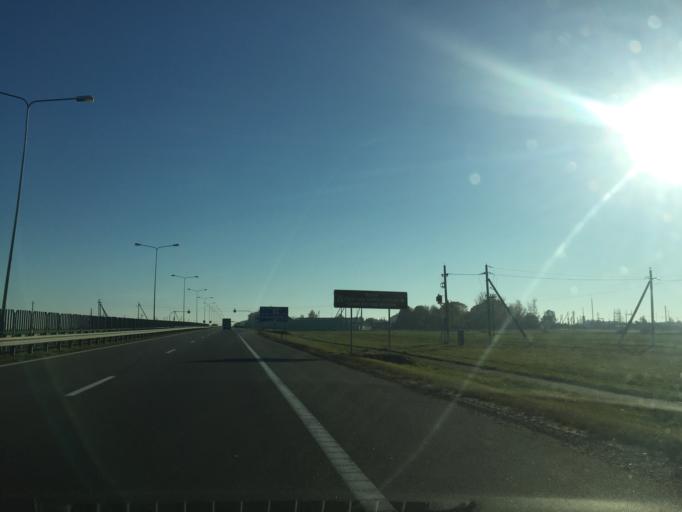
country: BY
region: Minsk
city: Smilavichy
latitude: 53.7595
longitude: 27.9997
